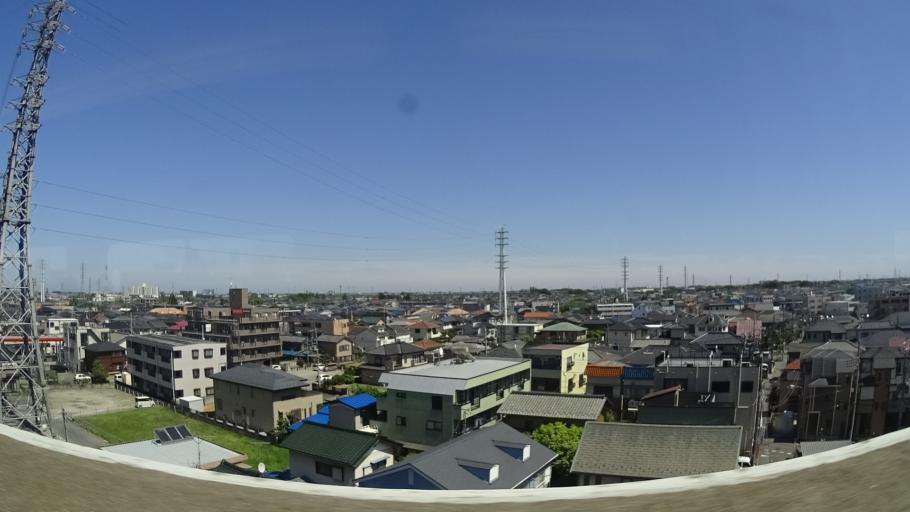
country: JP
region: Saitama
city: Kukichuo
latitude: 36.0677
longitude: 139.6791
